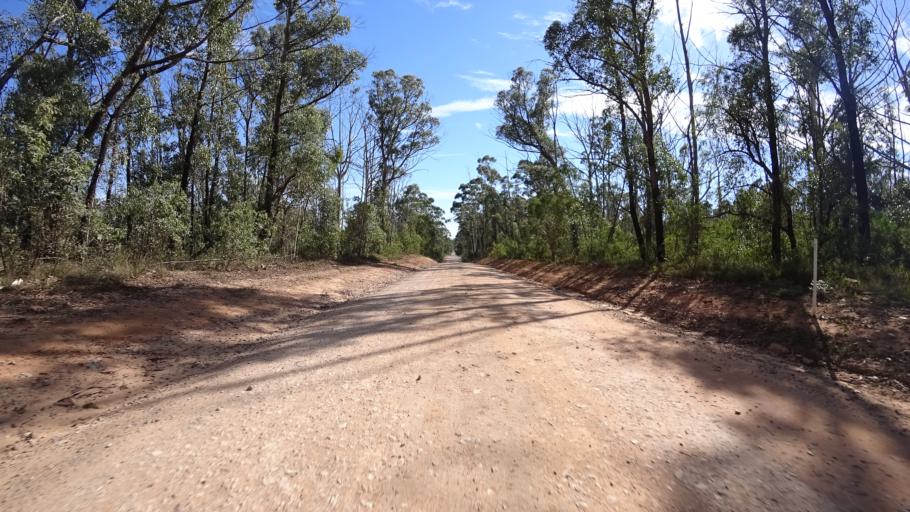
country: AU
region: New South Wales
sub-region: Lithgow
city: Lithgow
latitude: -33.4265
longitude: 150.2004
